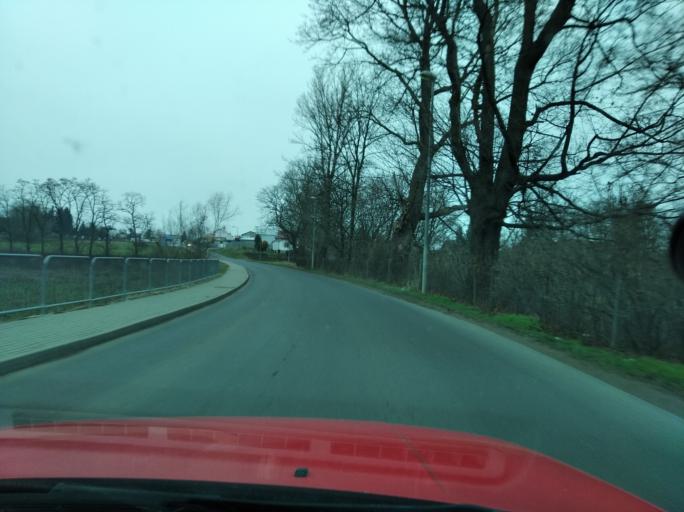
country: PL
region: Subcarpathian Voivodeship
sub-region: Powiat jaroslawski
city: Pawlosiow
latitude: 50.0094
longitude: 22.6536
